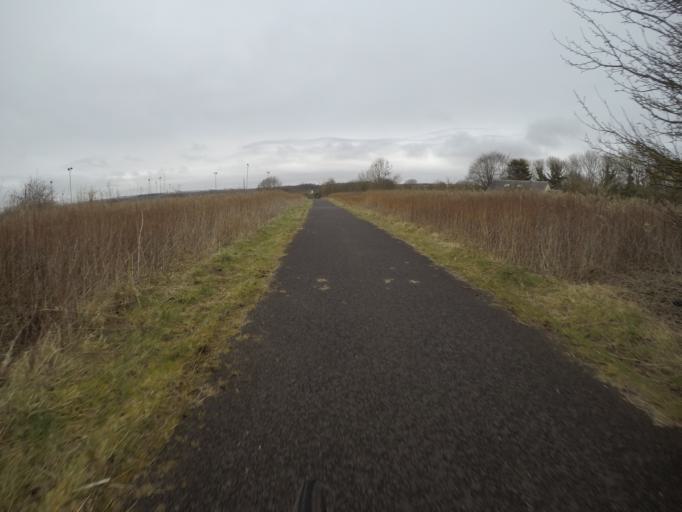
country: GB
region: Scotland
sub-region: North Ayrshire
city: Kilwinning
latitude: 55.6336
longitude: -4.6911
